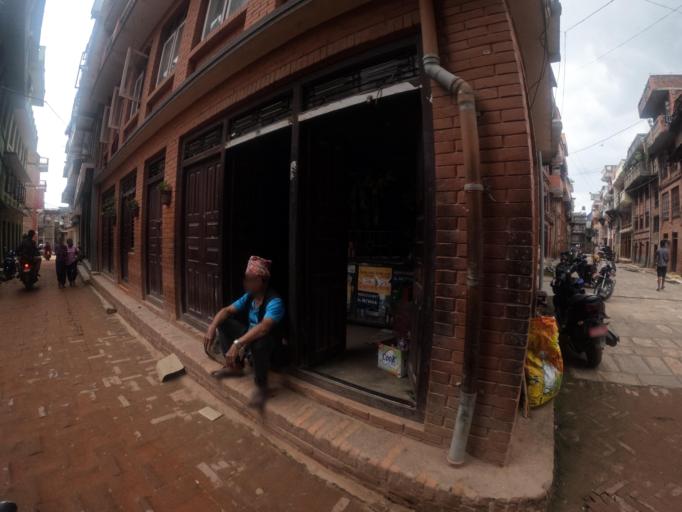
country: NP
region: Central Region
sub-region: Bagmati Zone
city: Bhaktapur
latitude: 27.6850
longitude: 85.3856
